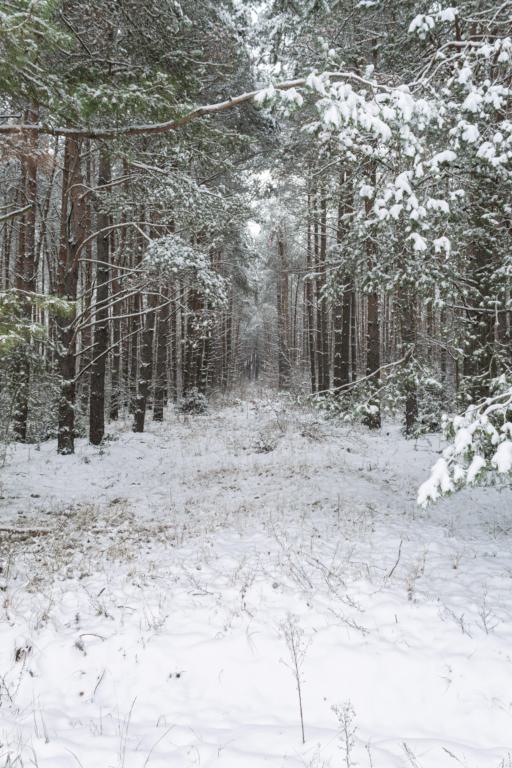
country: BY
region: Brest
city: Kamyanyets
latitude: 52.3725
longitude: 23.8451
